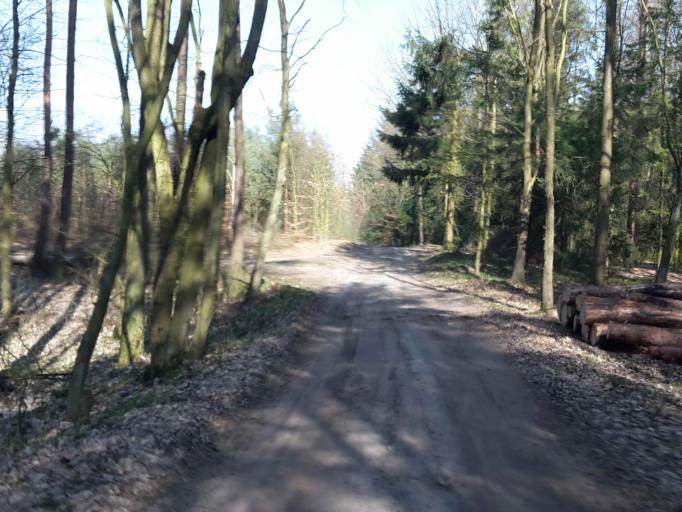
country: PL
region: Kujawsko-Pomorskie
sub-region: Powiat brodnicki
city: Brodnica
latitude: 53.3185
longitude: 19.3550
